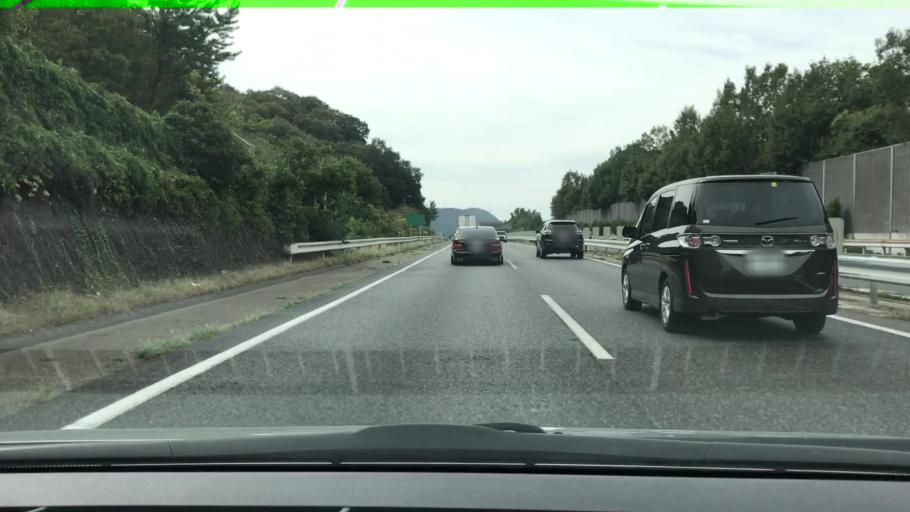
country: JP
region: Hyogo
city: Aioi
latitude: 34.8173
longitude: 134.4586
